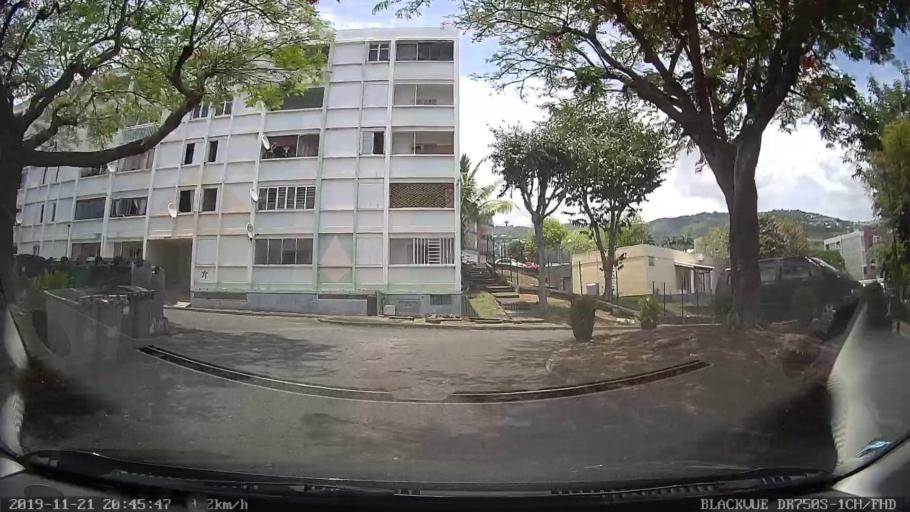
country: RE
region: Reunion
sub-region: Reunion
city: Saint-Denis
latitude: -20.8946
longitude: 55.4637
